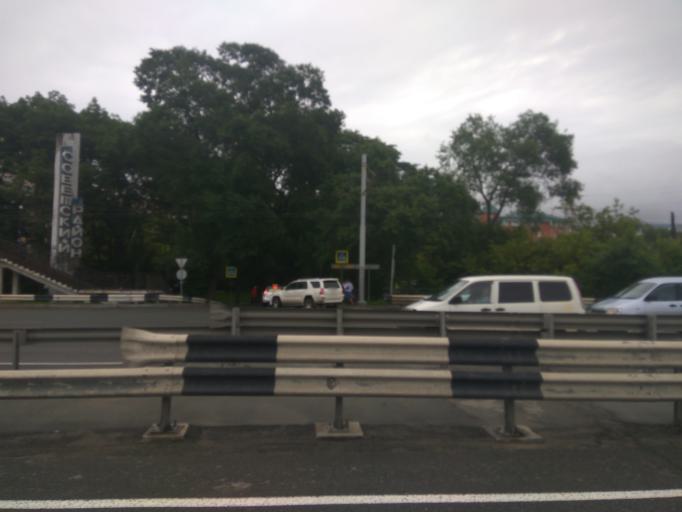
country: RU
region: Primorskiy
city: Vladivostok
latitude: 43.1644
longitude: 131.9136
